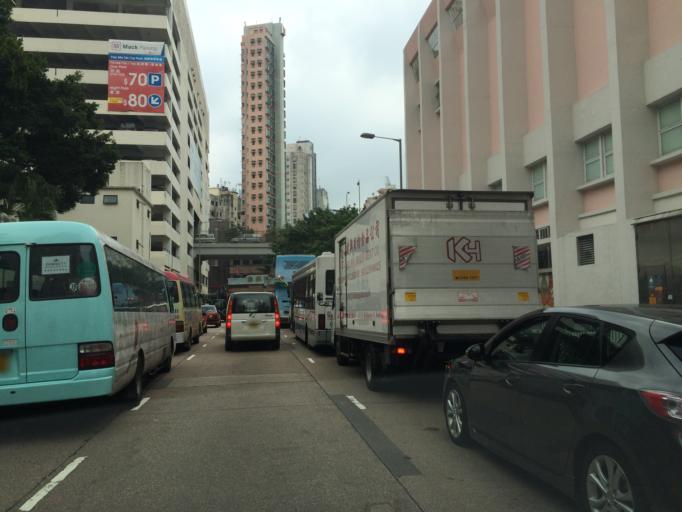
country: HK
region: Kowloon City
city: Kowloon
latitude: 22.3100
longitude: 114.1701
